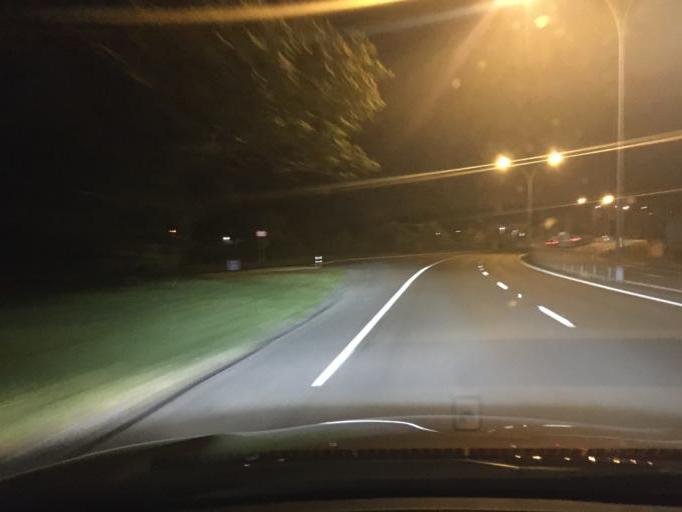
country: NZ
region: Waikato
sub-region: Hamilton City
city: Hamilton
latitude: -37.8127
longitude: 175.2828
